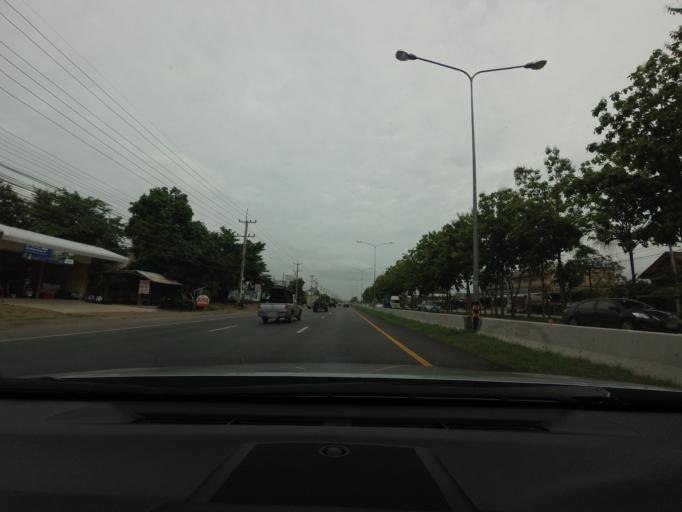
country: TH
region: Phetchaburi
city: Khao Yoi
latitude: 13.2337
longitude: 99.8240
